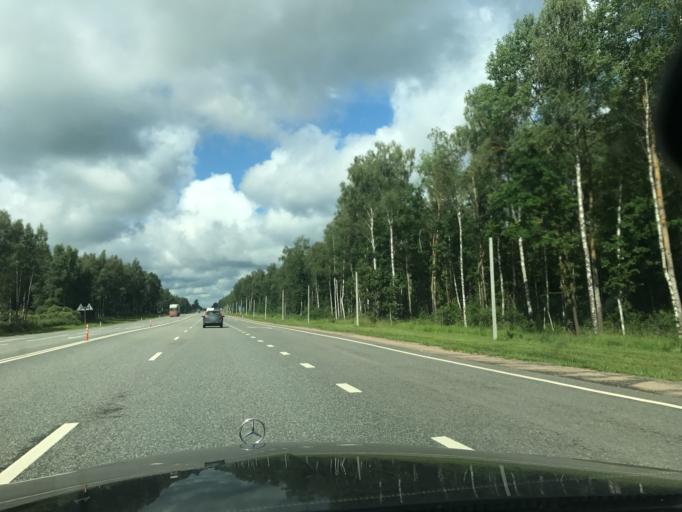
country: RU
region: Smolensk
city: Golynki
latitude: 54.7444
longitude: 31.4278
